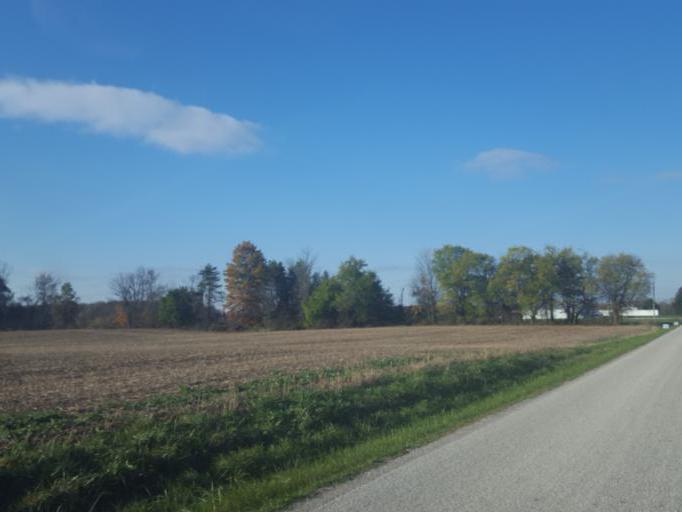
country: US
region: Ohio
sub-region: Crawford County
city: Galion
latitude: 40.6391
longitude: -82.7543
